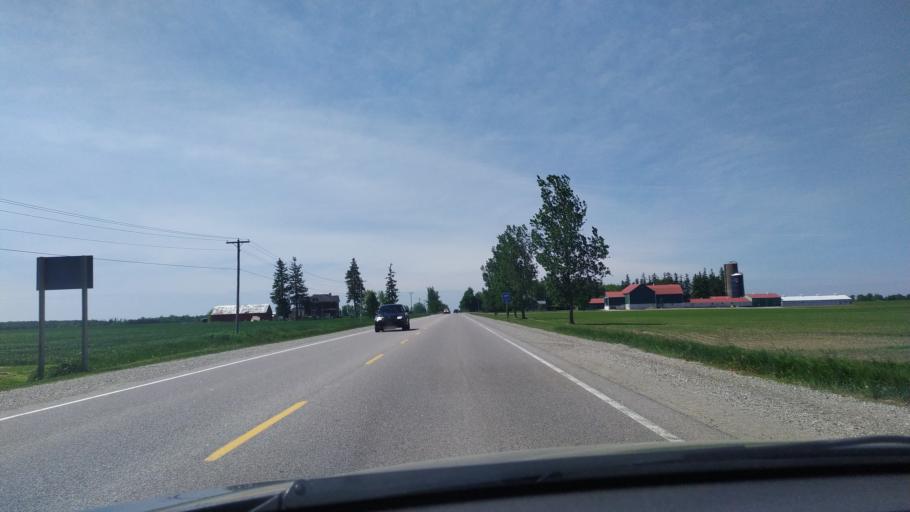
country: CA
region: Ontario
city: Stratford
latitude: 43.3365
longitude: -81.0123
